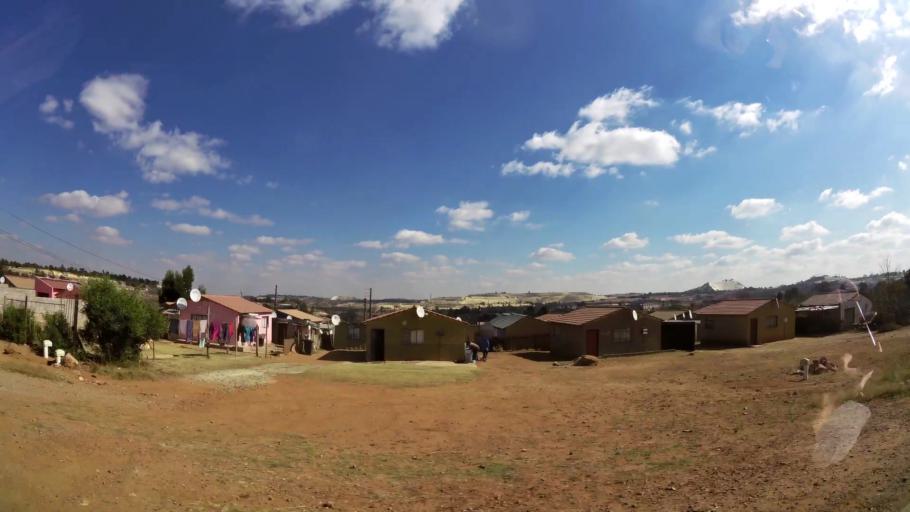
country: ZA
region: Gauteng
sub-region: West Rand District Municipality
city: Krugersdorp
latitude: -26.1376
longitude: 27.7867
